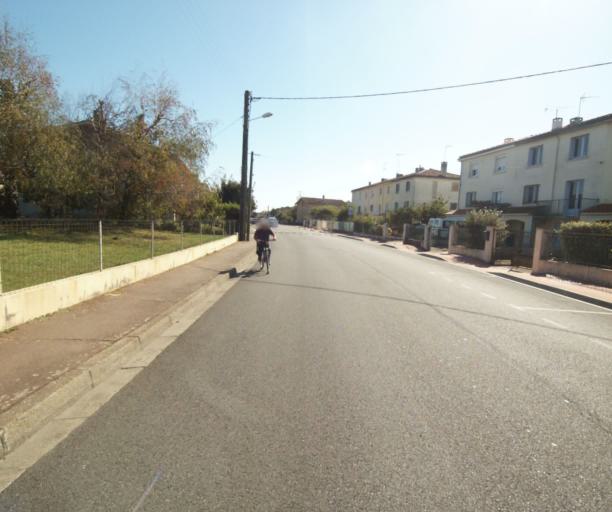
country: FR
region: Midi-Pyrenees
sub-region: Departement du Tarn-et-Garonne
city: Moissac
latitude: 44.1047
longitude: 1.0955
